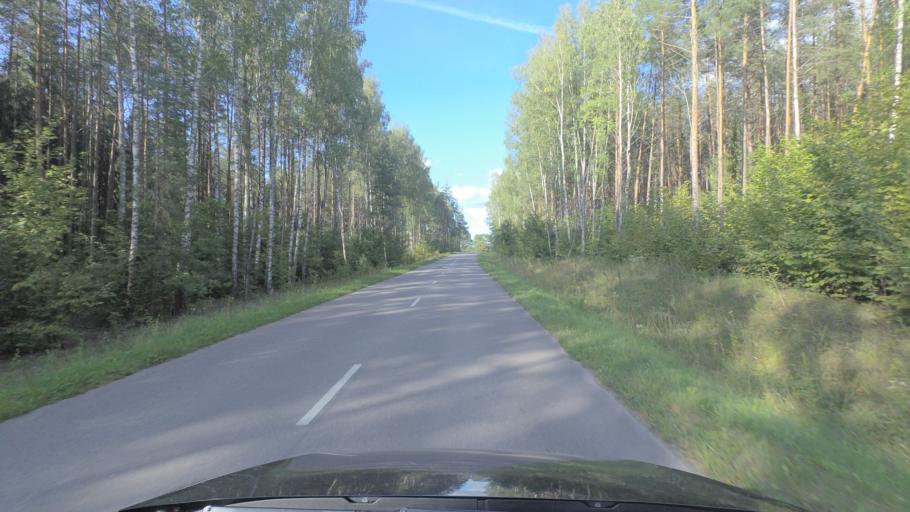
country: LT
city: Pabrade
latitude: 55.0871
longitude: 25.6842
